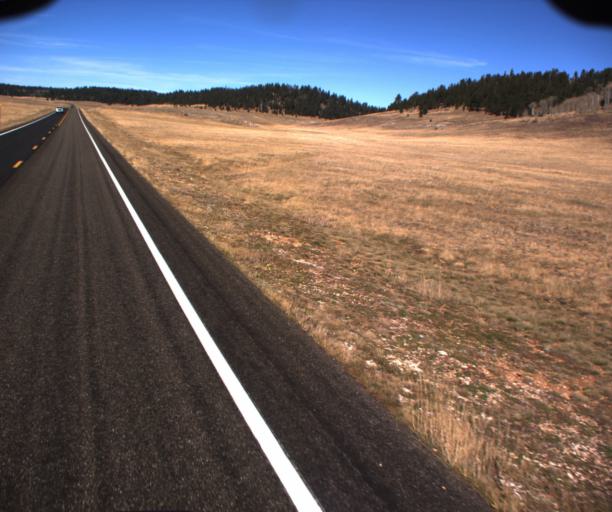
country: US
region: Arizona
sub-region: Coconino County
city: Grand Canyon
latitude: 36.4788
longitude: -112.1265
